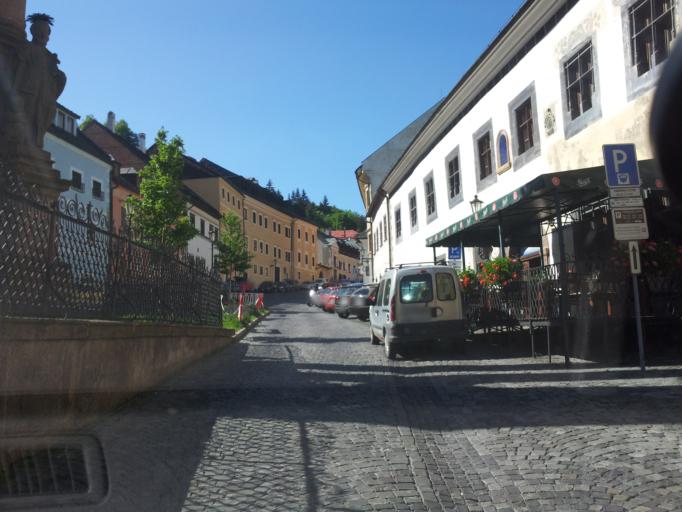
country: SK
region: Banskobystricky
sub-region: Okres Banska Bystrica
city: Banska Stiavnica
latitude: 48.4597
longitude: 18.8926
